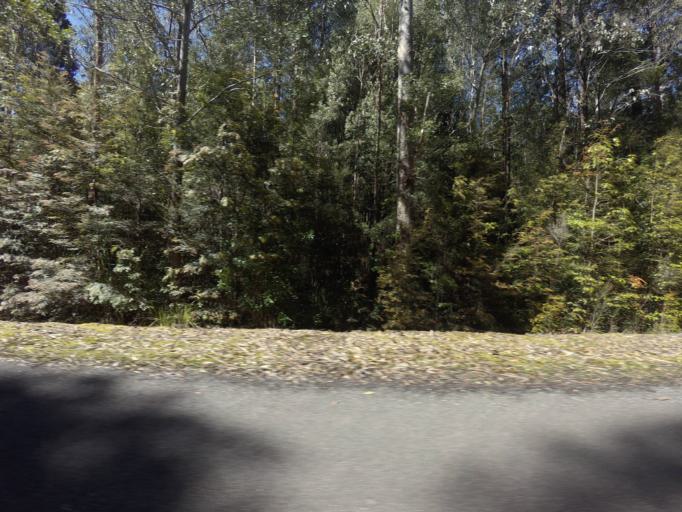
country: AU
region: Tasmania
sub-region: Huon Valley
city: Geeveston
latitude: -42.8211
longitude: 146.3328
